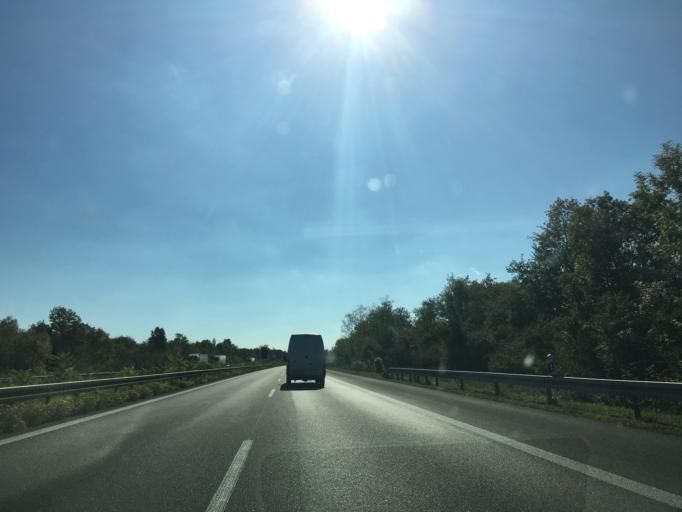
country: DE
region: Baden-Wuerttemberg
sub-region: Freiburg Region
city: Neuenburg am Rhein
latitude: 47.8441
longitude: 7.5669
